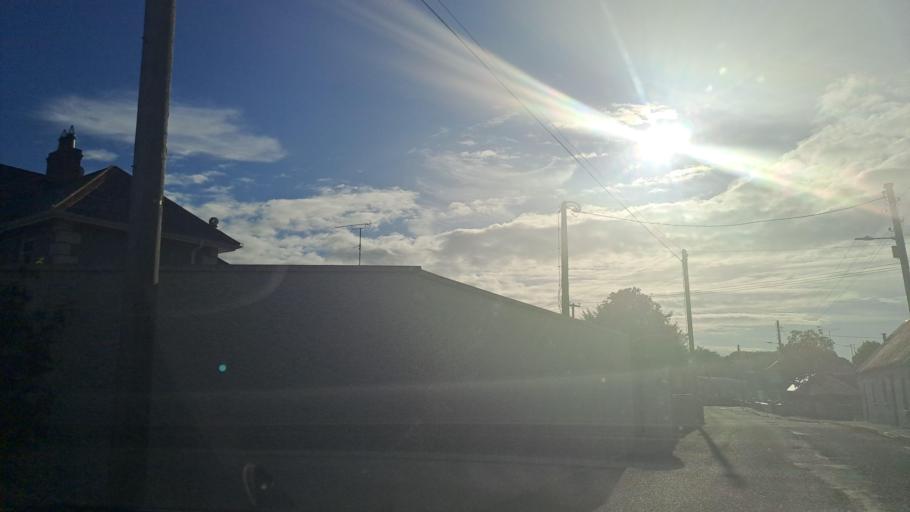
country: IE
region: Ulster
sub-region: County Monaghan
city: Carrickmacross
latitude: 53.9749
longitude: -6.7224
